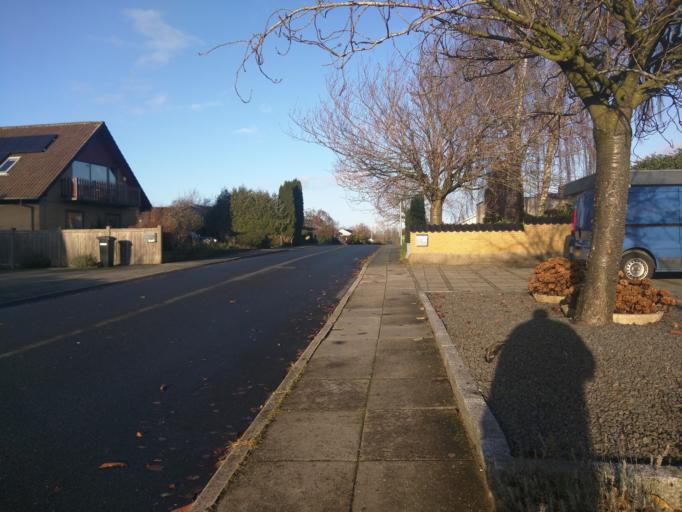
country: DK
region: Central Jutland
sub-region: Silkeborg Kommune
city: Silkeborg
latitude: 56.1853
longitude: 9.5242
